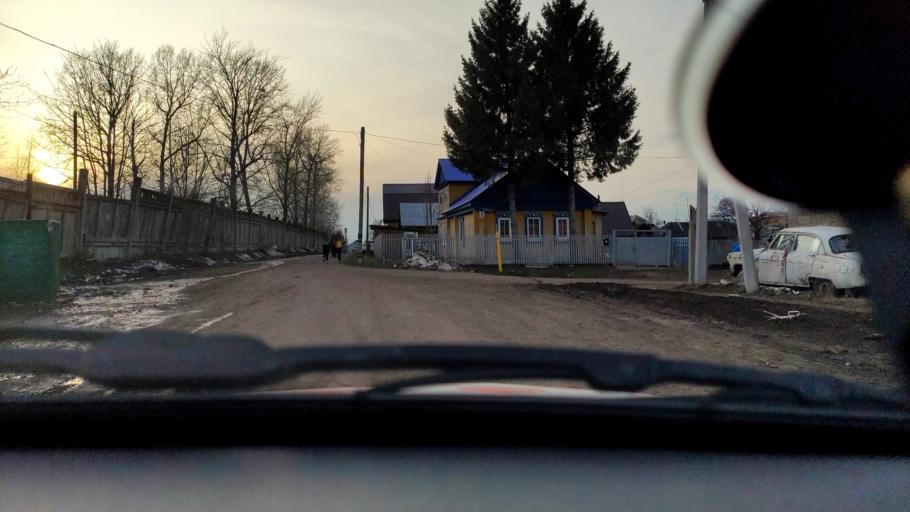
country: RU
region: Bashkortostan
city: Ufa
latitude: 54.8346
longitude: 56.1523
